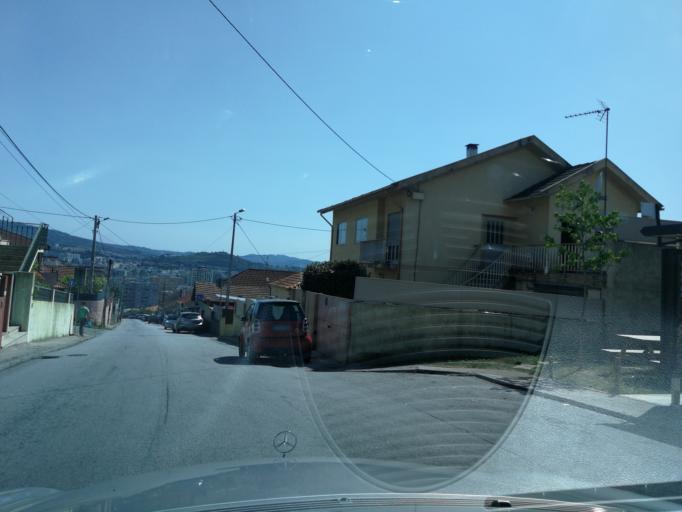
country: PT
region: Braga
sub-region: Braga
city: Braga
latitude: 41.5642
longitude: -8.4036
